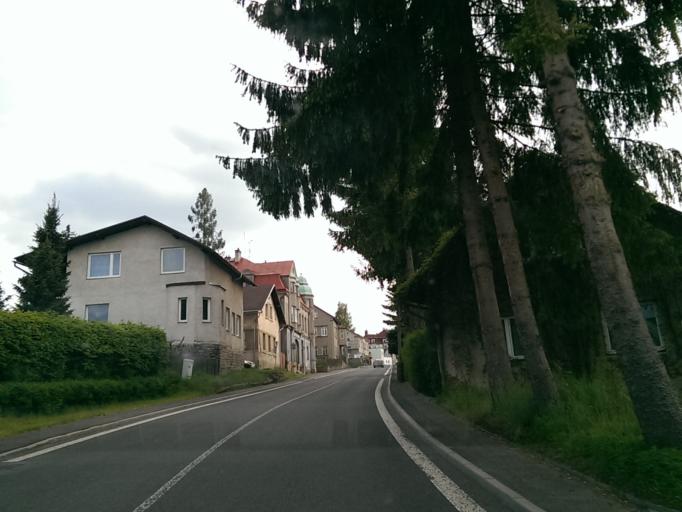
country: CZ
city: Plavy
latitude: 50.6888
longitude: 15.3074
